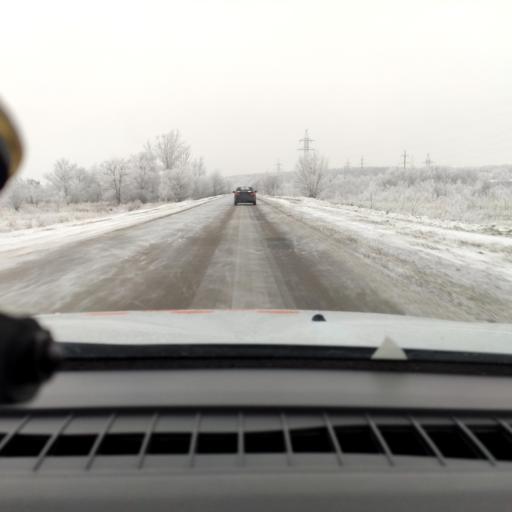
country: RU
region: Samara
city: Samara
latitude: 53.1097
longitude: 50.2256
